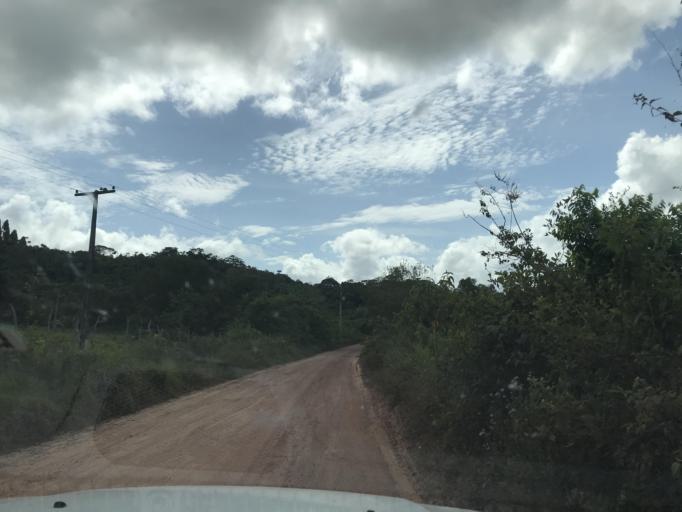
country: BR
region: Bahia
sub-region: Entre Rios
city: Entre Rios
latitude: -12.1696
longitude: -38.0655
